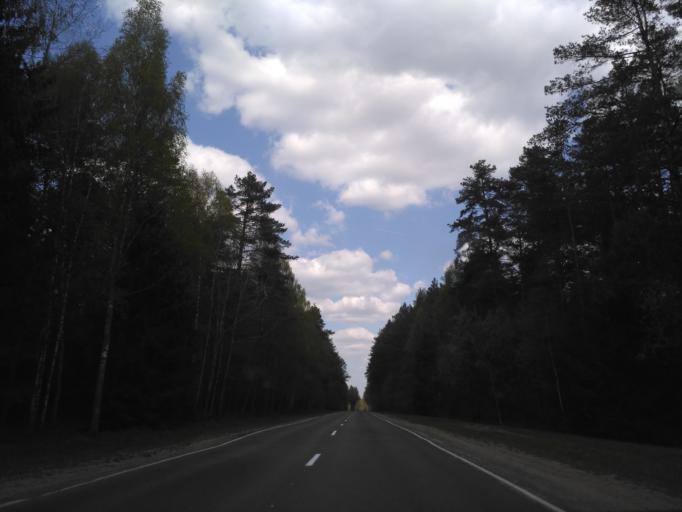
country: BY
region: Minsk
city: Myadzyel
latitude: 54.7295
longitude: 26.9403
